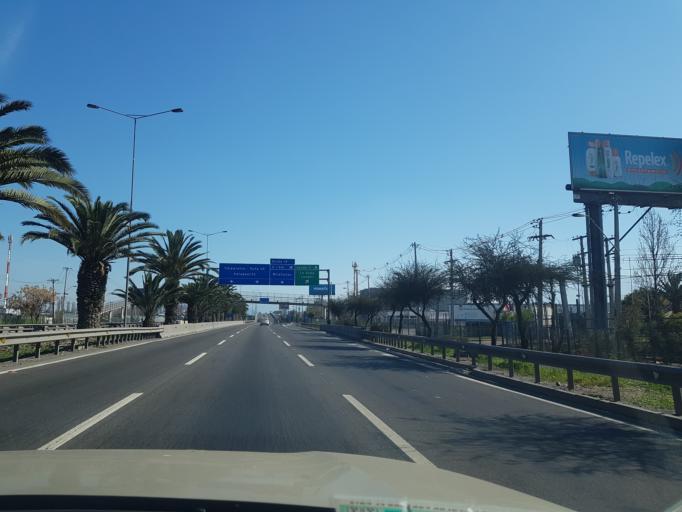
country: CL
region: Santiago Metropolitan
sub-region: Provincia de Santiago
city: Lo Prado
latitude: -33.3830
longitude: -70.7561
